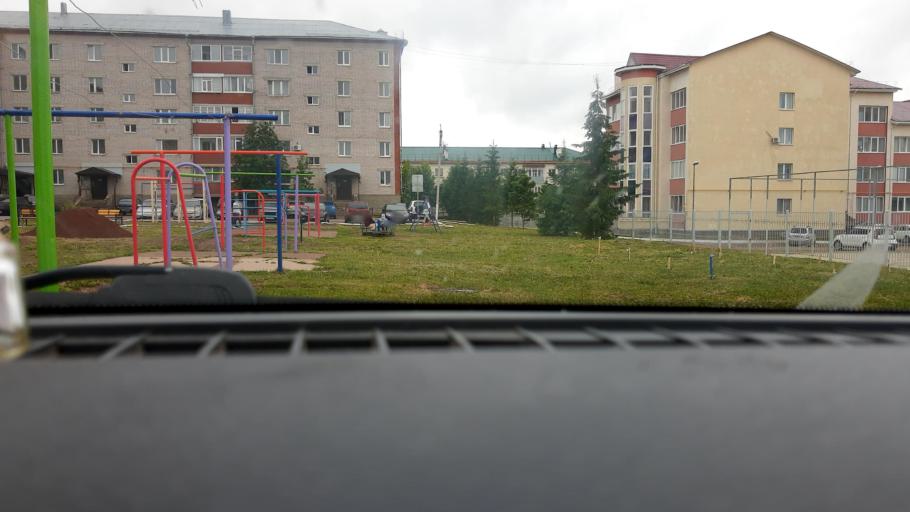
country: RU
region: Bashkortostan
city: Priyutovo
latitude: 53.9064
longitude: 53.9336
